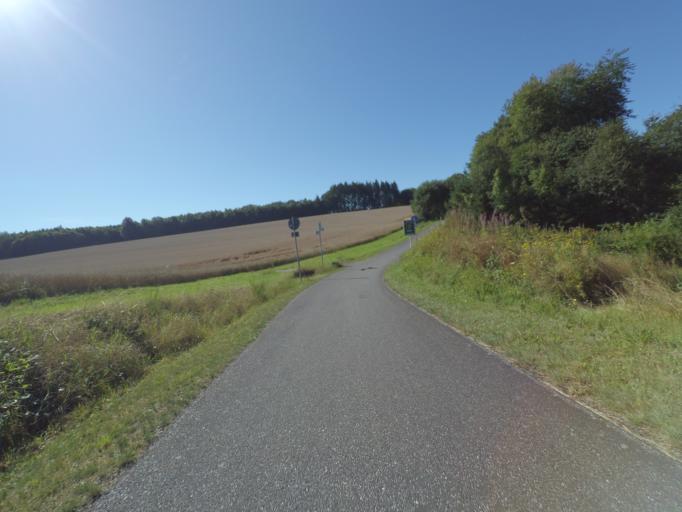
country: DE
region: Rheinland-Pfalz
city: Eckfeld
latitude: 50.1029
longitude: 6.8419
